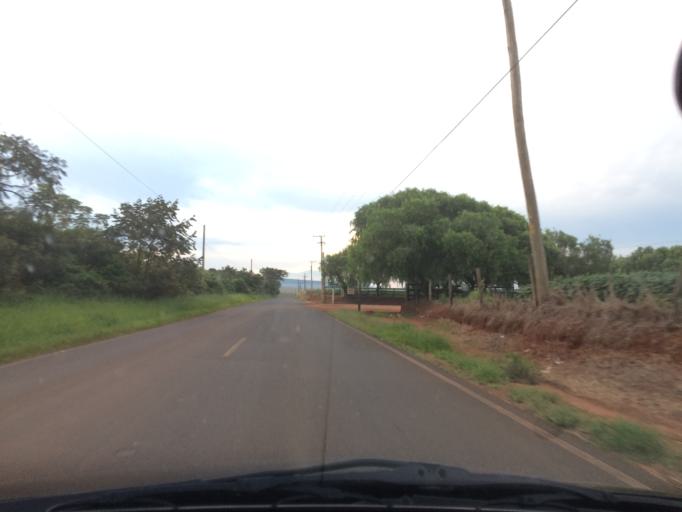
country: BR
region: Sao Paulo
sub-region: Casa Branca
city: Casa Branca
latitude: -21.7509
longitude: -47.1353
